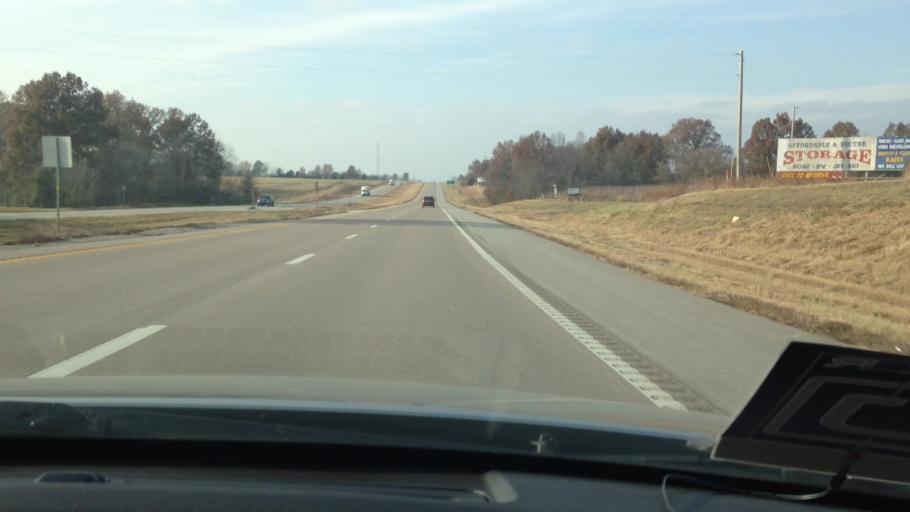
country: US
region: Missouri
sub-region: Cass County
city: Garden City
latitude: 38.4698
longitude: -94.0114
